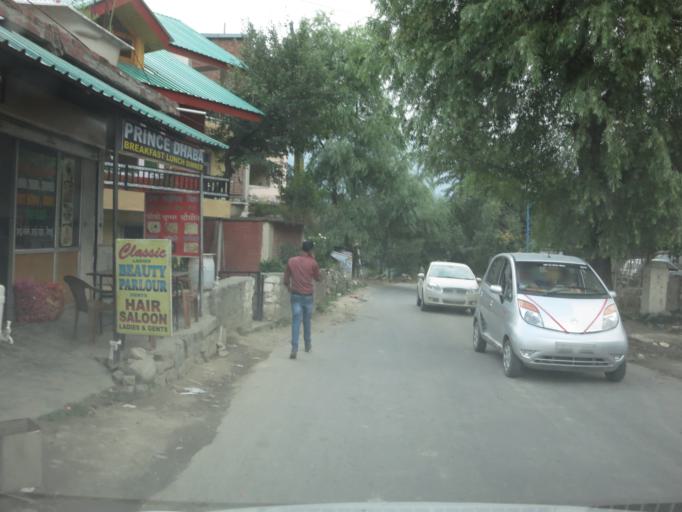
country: IN
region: Himachal Pradesh
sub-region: Kulu
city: Manali
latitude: 32.2246
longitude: 77.1958
